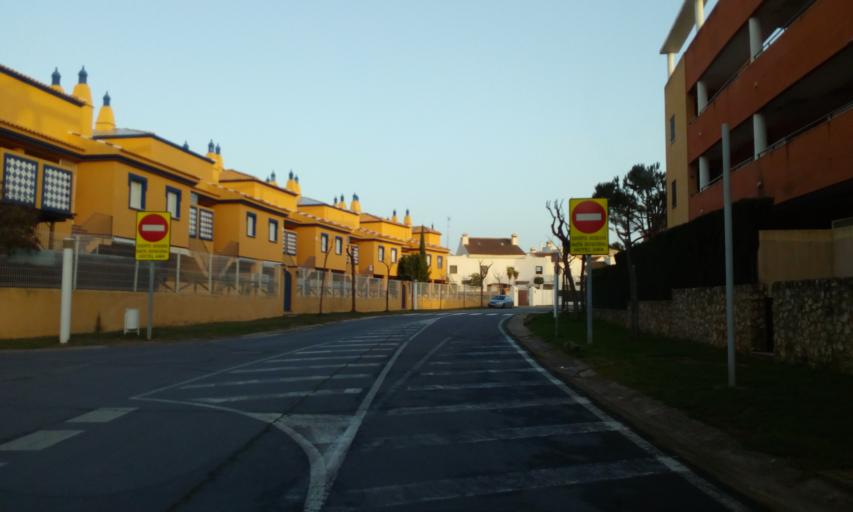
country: ES
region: Andalusia
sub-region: Provincia de Huelva
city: Lepe
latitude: 37.2157
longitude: -7.2284
